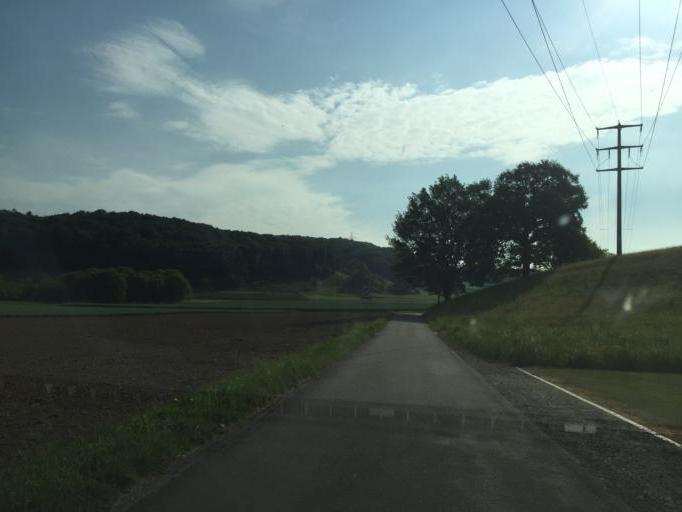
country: CH
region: Zurich
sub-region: Bezirk Buelach
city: Buelach / Soligaenter
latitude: 47.5303
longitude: 8.5450
